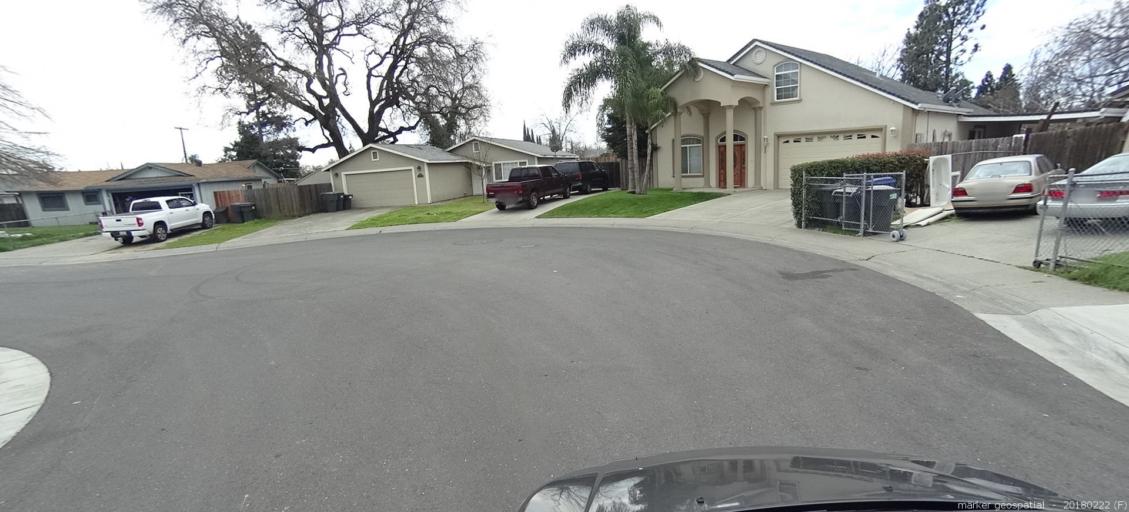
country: US
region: California
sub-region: Sacramento County
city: Rio Linda
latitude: 38.7165
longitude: -121.4105
